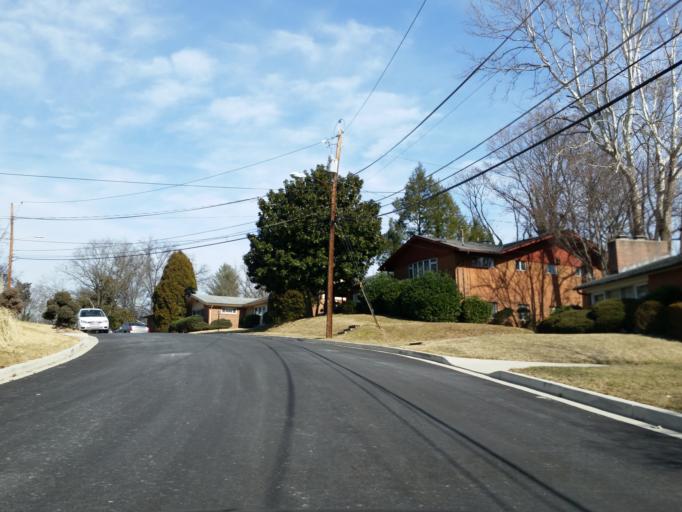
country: US
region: Maryland
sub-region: Montgomery County
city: Silver Spring
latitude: 38.9907
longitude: -77.0419
